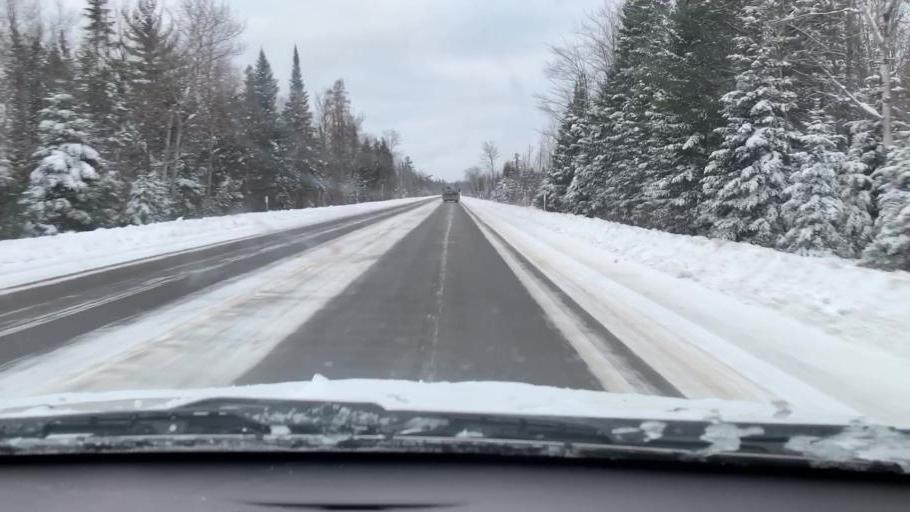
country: US
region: Michigan
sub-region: Kalkaska County
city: Kalkaska
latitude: 44.7105
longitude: -85.1952
